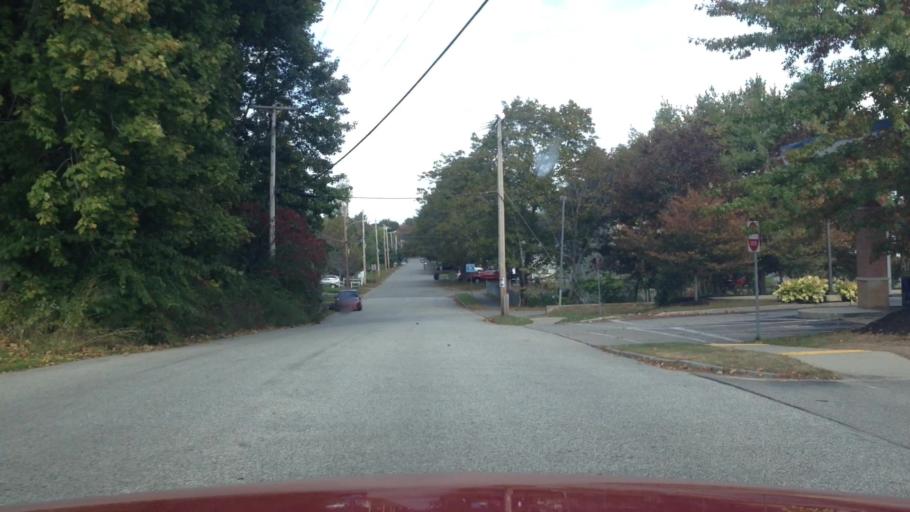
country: US
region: Maine
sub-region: Cumberland County
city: South Portland Gardens
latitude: 43.6754
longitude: -70.3234
